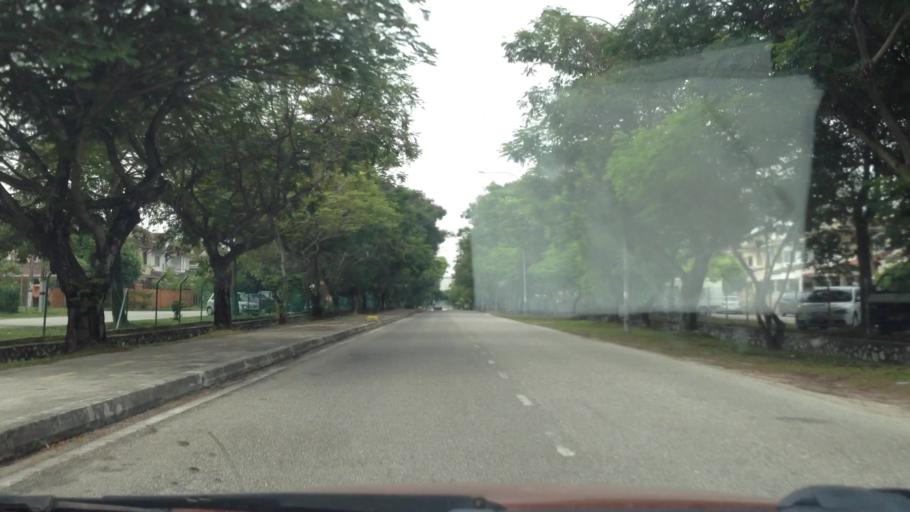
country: MY
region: Selangor
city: Subang Jaya
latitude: 3.0518
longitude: 101.5739
